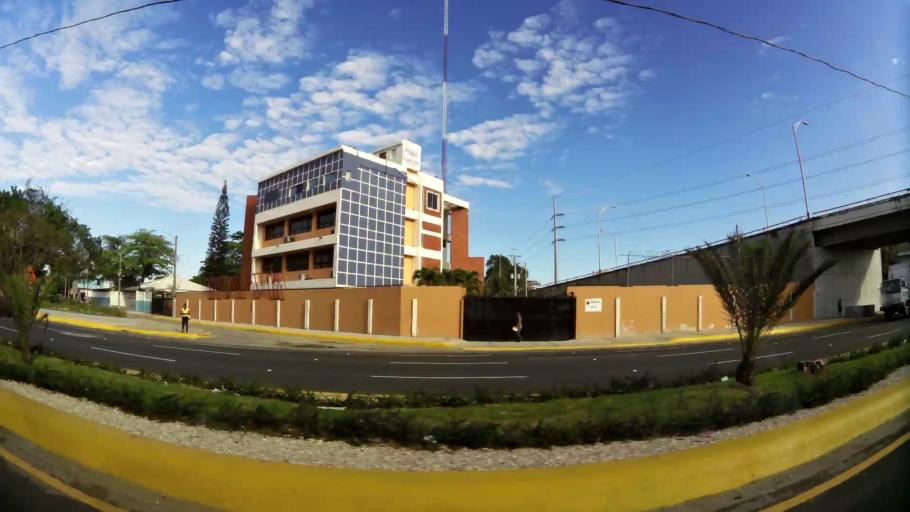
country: DO
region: Nacional
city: San Carlos
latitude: 18.4915
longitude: -69.9019
